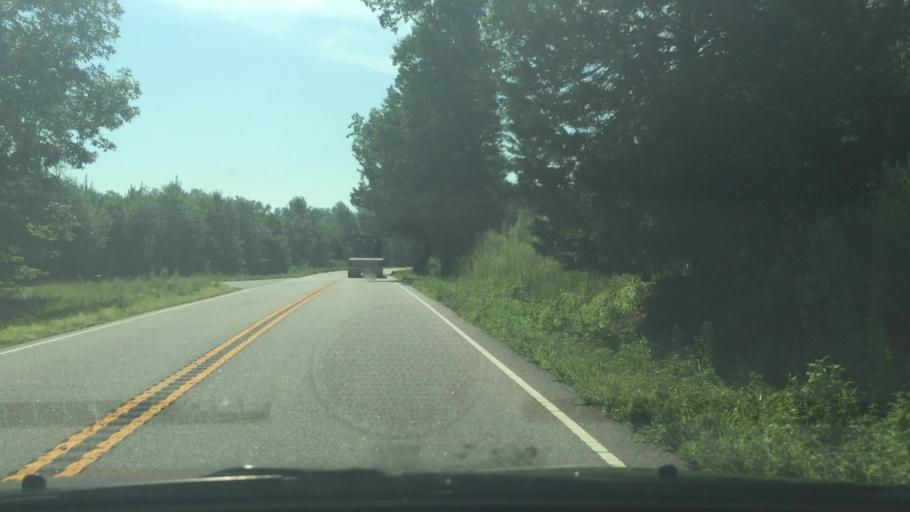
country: US
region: Virginia
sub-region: Sussex County
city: Sussex
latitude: 37.0124
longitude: -77.2758
